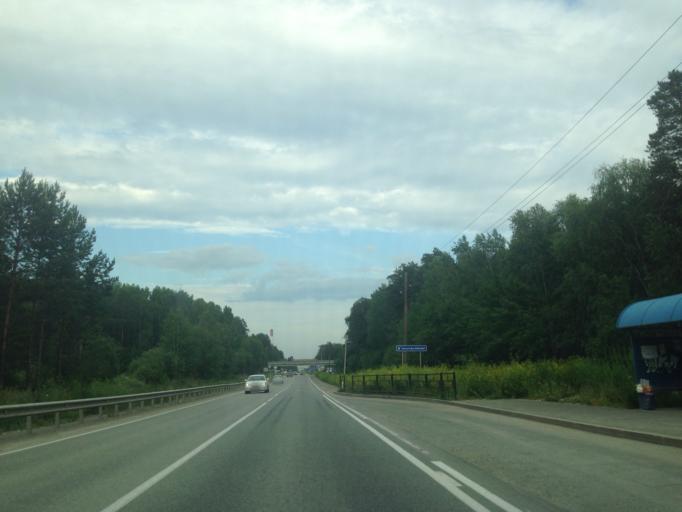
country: RU
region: Sverdlovsk
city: Istok
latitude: 56.8393
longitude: 60.7955
